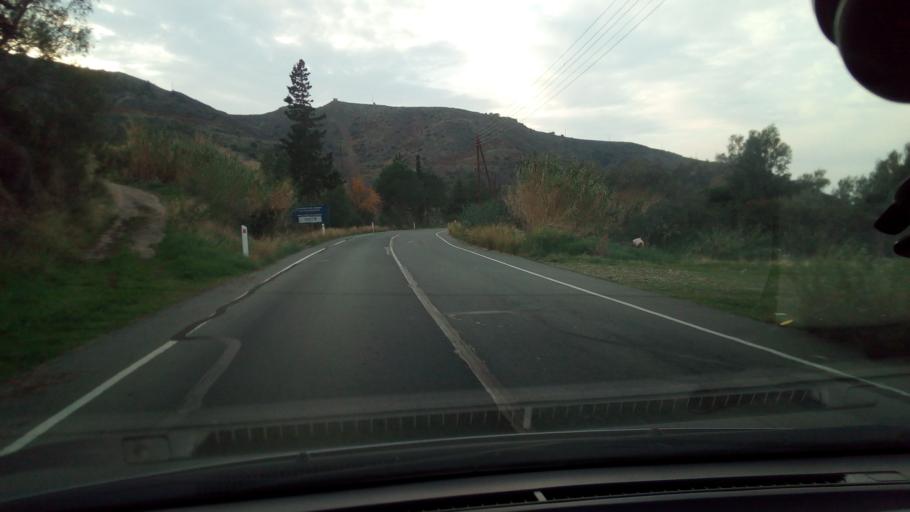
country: CY
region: Lefkosia
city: Kato Pyrgos
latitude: 35.1684
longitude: 32.5660
